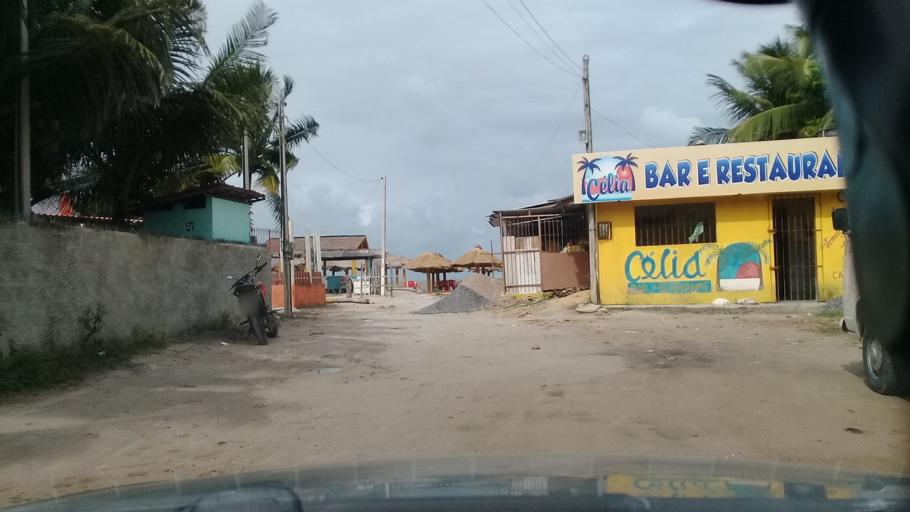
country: BR
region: Pernambuco
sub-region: Itamaraca
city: Itamaraca
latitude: -7.7549
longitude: -34.8248
